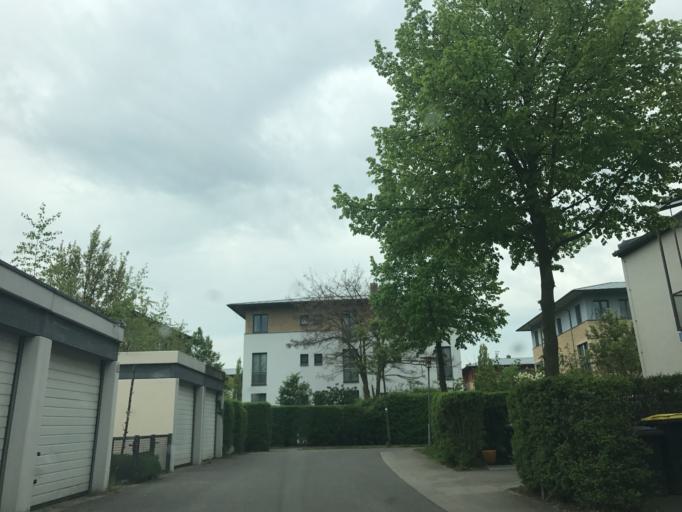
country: DE
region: Berlin
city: Staaken
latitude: 52.5587
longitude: 13.1402
